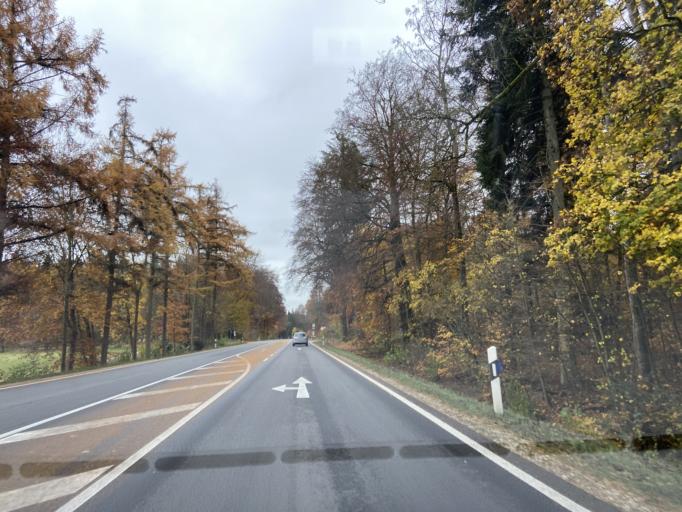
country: DE
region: Baden-Wuerttemberg
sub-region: Tuebingen Region
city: Krauchenwies
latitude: 48.0564
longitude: 9.2312
